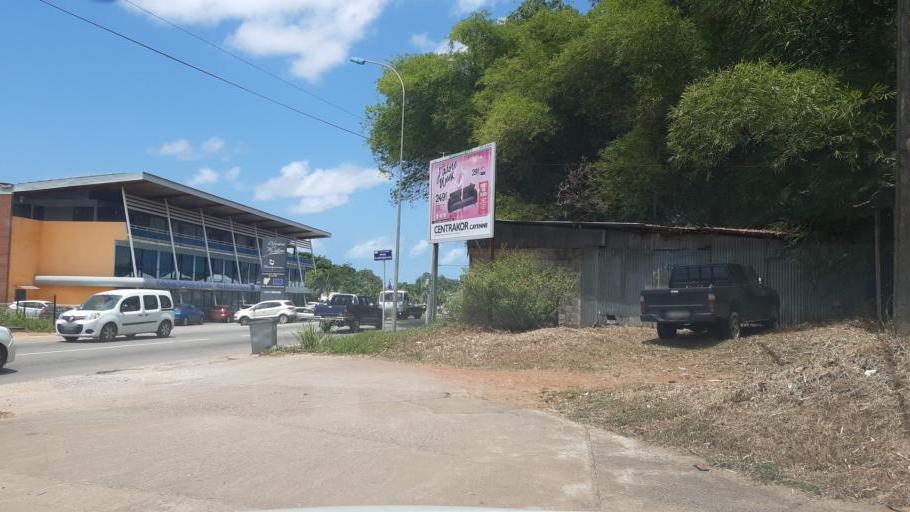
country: GF
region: Guyane
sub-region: Guyane
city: Cayenne
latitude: 4.9122
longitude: -52.3211
